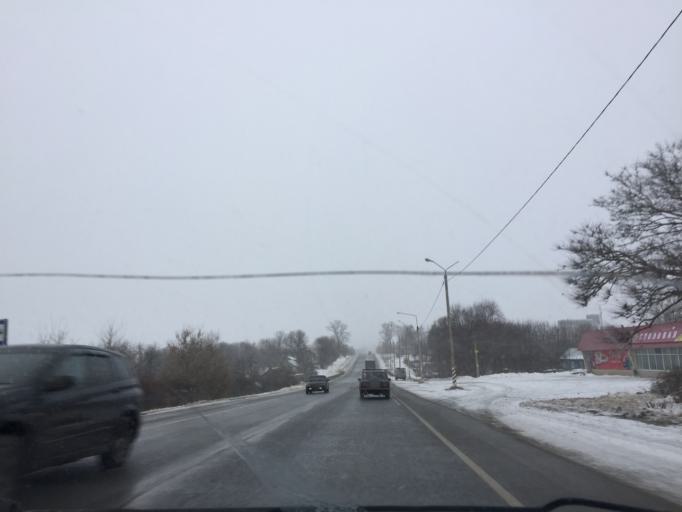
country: RU
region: Tula
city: Plavsk
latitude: 53.8137
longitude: 37.3933
